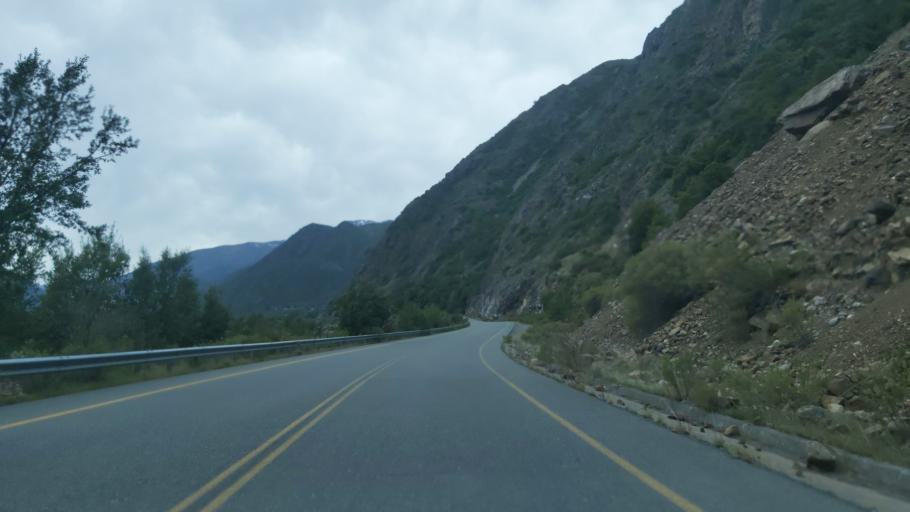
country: CL
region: Maule
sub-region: Provincia de Linares
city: Colbun
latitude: -35.8025
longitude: -70.8933
